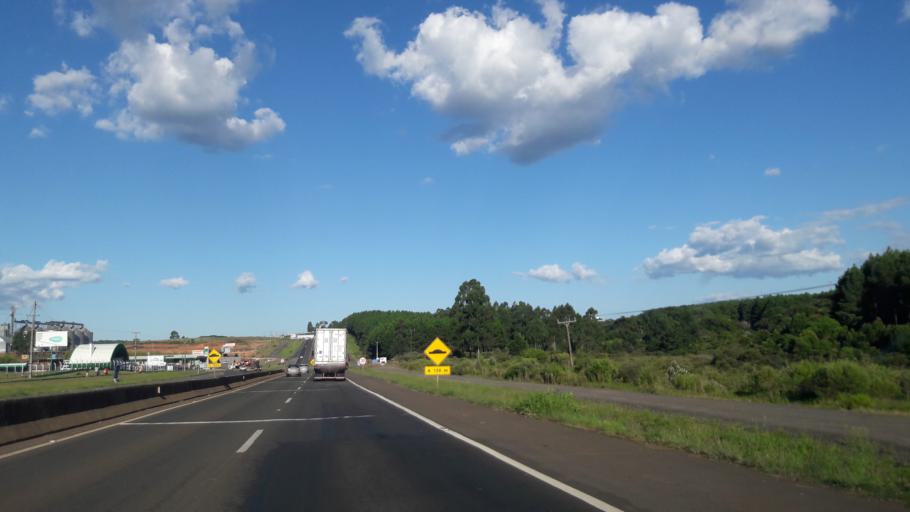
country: BR
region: Parana
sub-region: Guarapuava
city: Guarapuava
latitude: -25.3456
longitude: -51.4449
